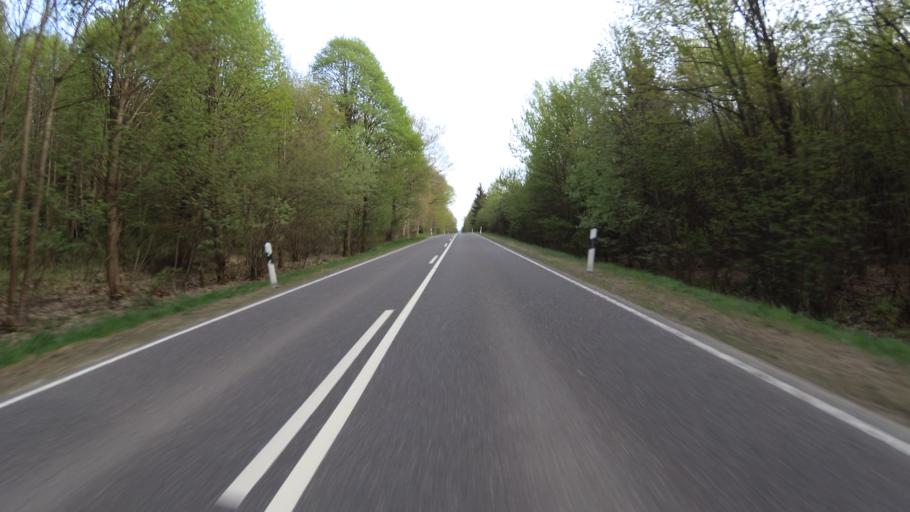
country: DE
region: Rheinland-Pfalz
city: Morbach
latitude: 49.8415
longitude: 7.1199
